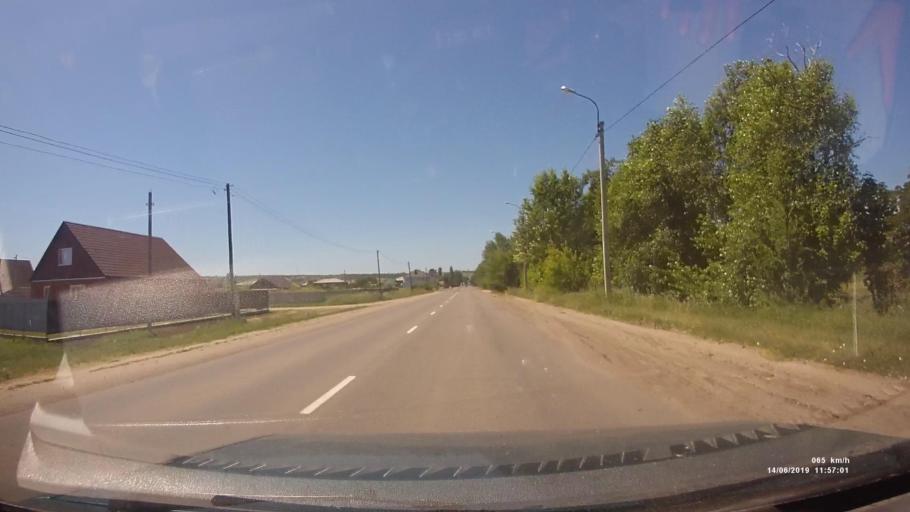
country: RU
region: Rostov
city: Kazanskaya
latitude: 49.8003
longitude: 41.1538
